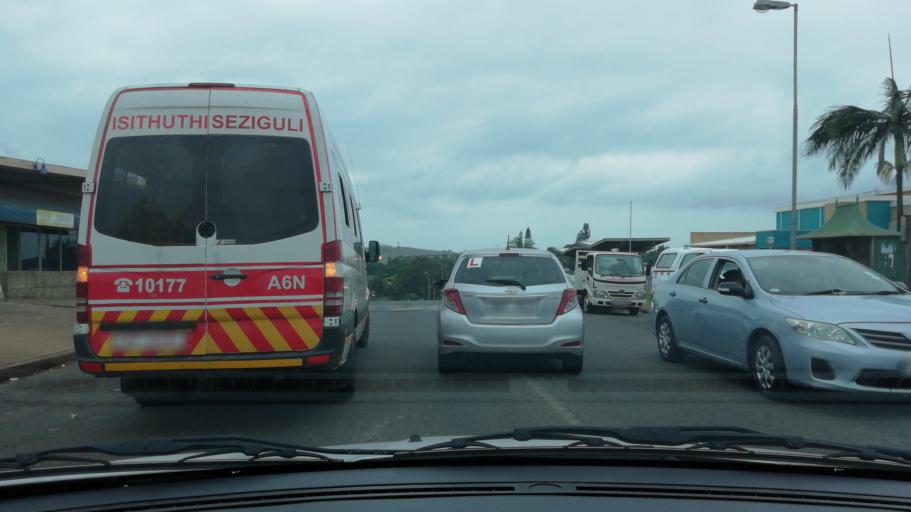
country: ZA
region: KwaZulu-Natal
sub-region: uThungulu District Municipality
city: Empangeni
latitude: -28.7398
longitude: 31.8953
